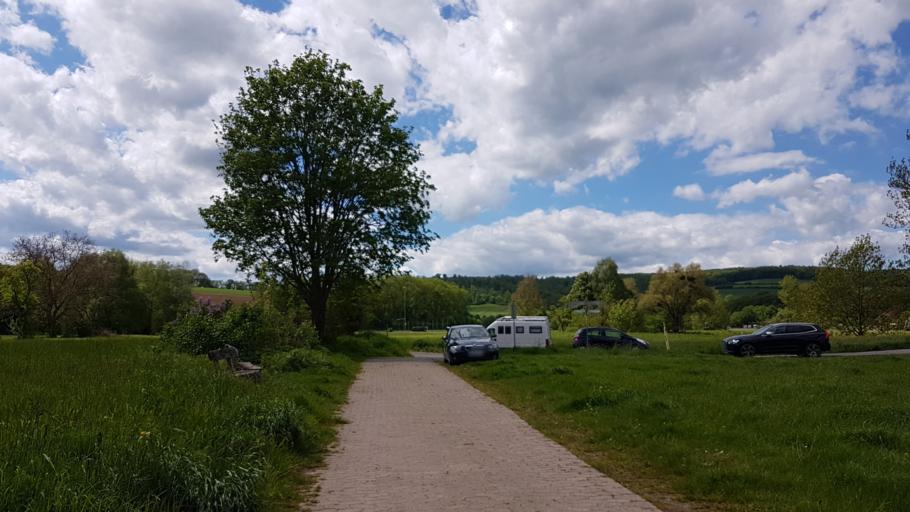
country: DE
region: Lower Saxony
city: Ottenstein
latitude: 52.0117
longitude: 9.3464
